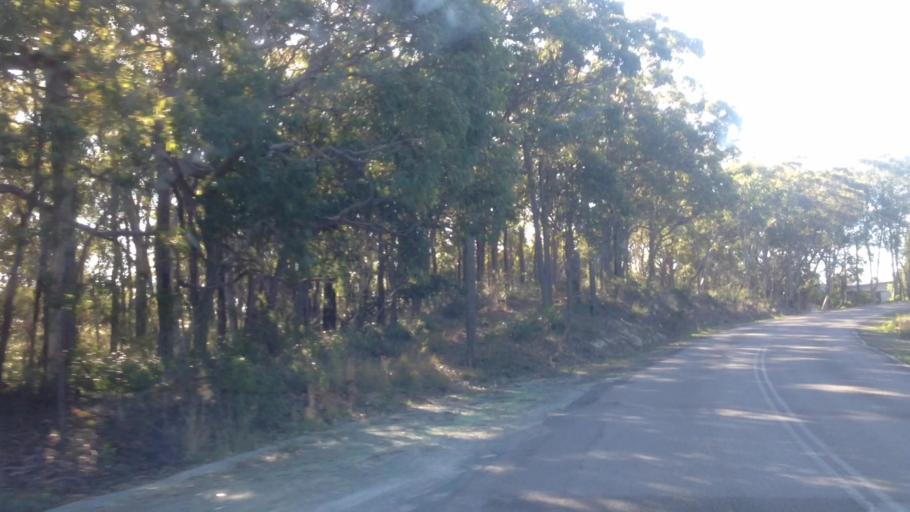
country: AU
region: New South Wales
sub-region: Lake Macquarie Shire
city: Arcadia vale
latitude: -33.1097
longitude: 151.5593
